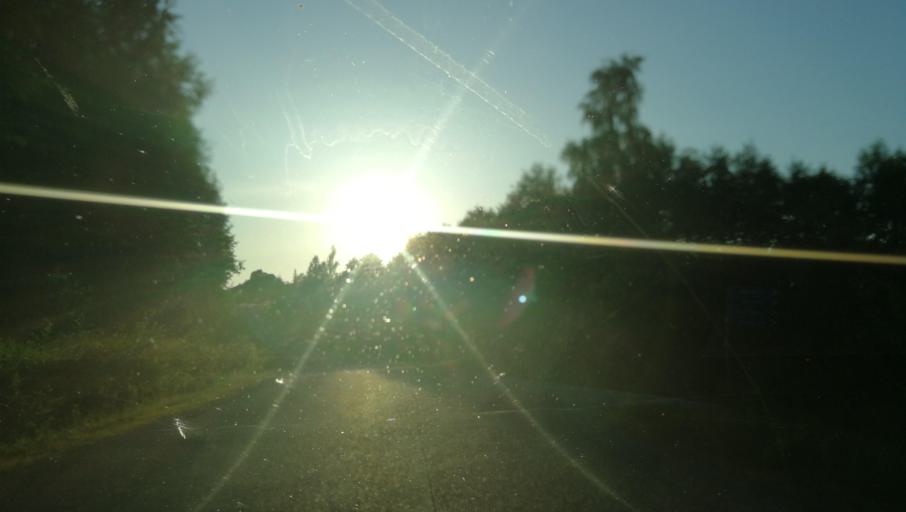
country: LV
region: Priekuli
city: Priekuli
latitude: 57.2589
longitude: 25.3669
